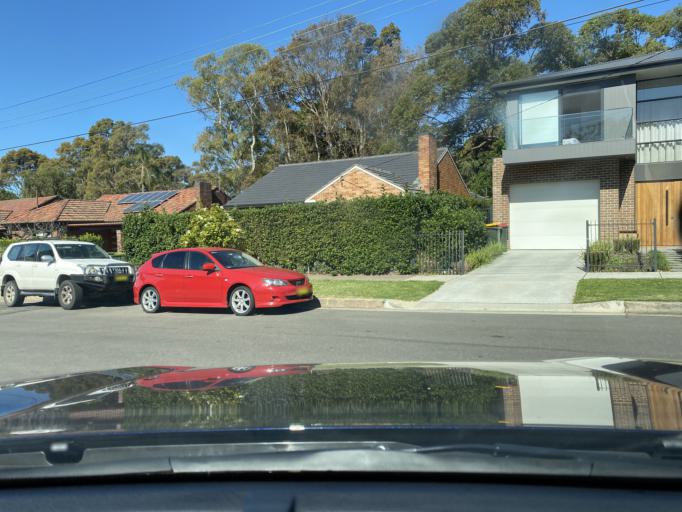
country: AU
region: New South Wales
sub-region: Canada Bay
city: Wareemba
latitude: -33.8541
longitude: 151.1327
